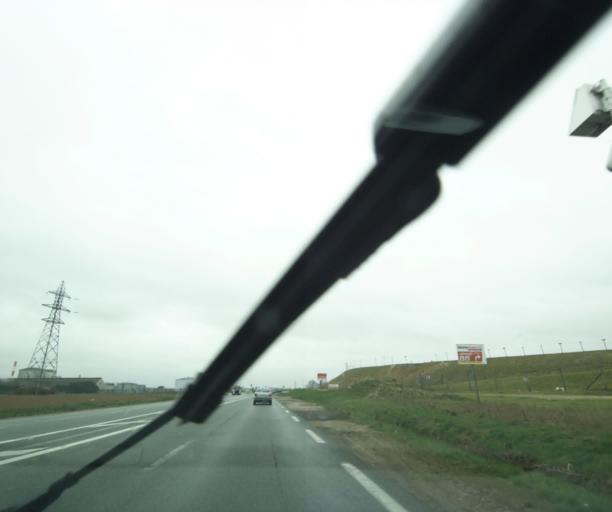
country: FR
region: Centre
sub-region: Departement du Loiret
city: Artenay
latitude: 48.0987
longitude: 1.8850
